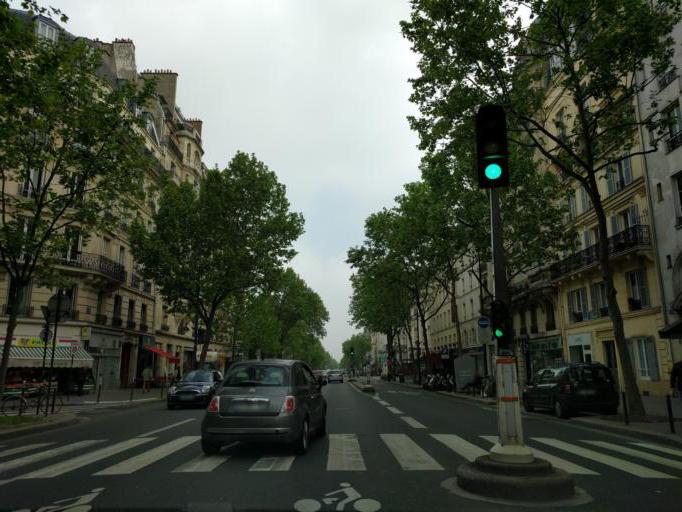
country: FR
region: Ile-de-France
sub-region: Paris
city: Paris
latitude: 48.8434
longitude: 2.3383
